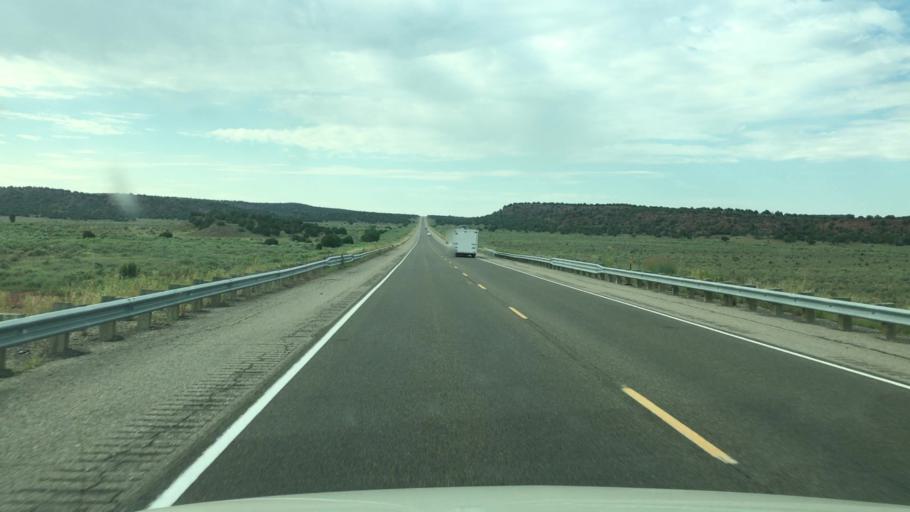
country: US
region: New Mexico
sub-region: Santa Fe County
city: Eldorado at Santa Fe
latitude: 35.2497
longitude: -105.8074
